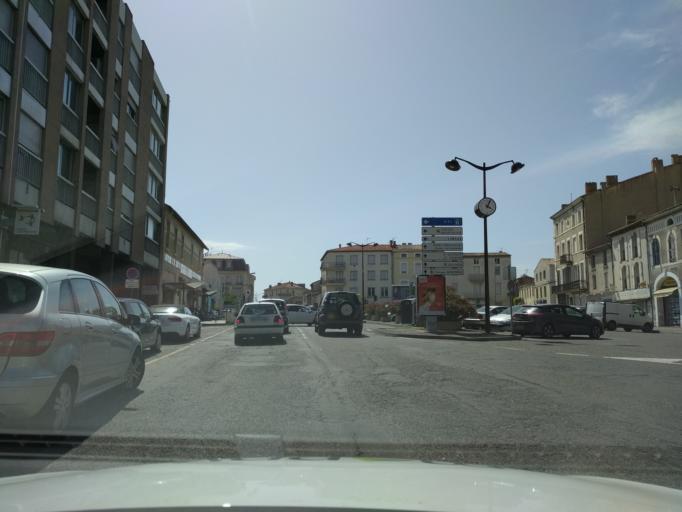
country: FR
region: Languedoc-Roussillon
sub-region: Departement de l'Aude
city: Carcassonne
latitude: 43.2126
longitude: 2.3461
